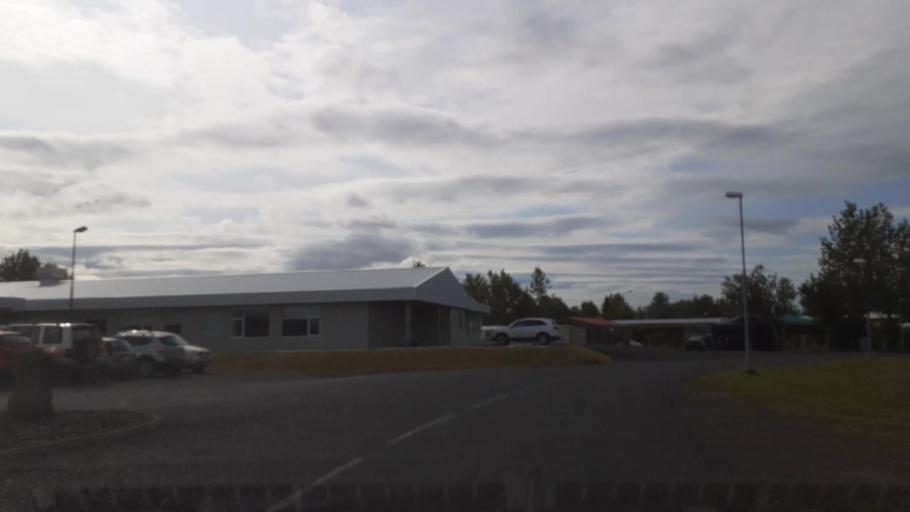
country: IS
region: South
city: Vestmannaeyjar
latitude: 63.8433
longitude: -20.3973
